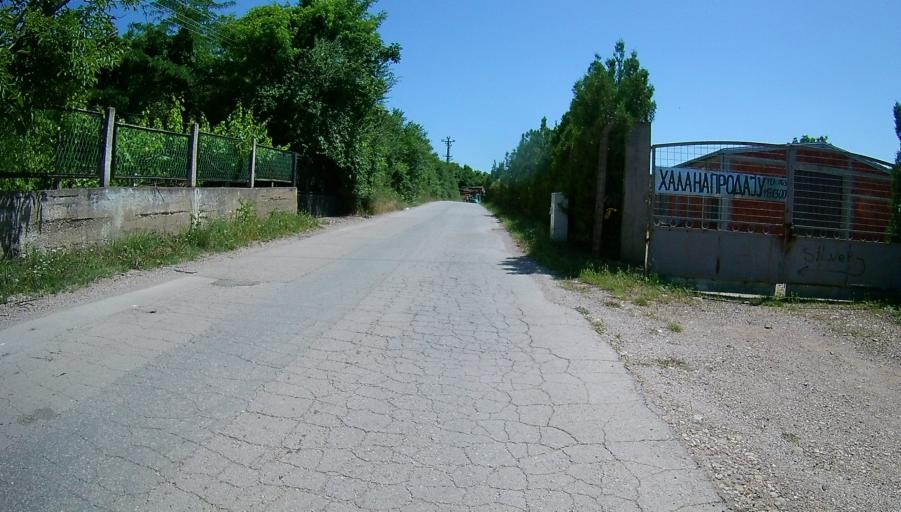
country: RS
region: Central Serbia
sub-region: Nisavski Okrug
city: Nis
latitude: 43.2911
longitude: 21.9011
